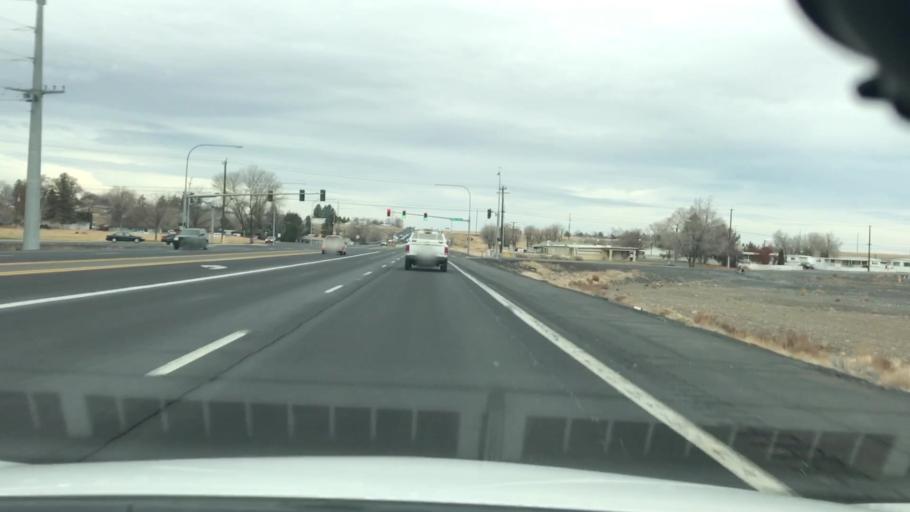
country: US
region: Washington
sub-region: Grant County
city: Moses Lake
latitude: 47.1491
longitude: -119.2926
